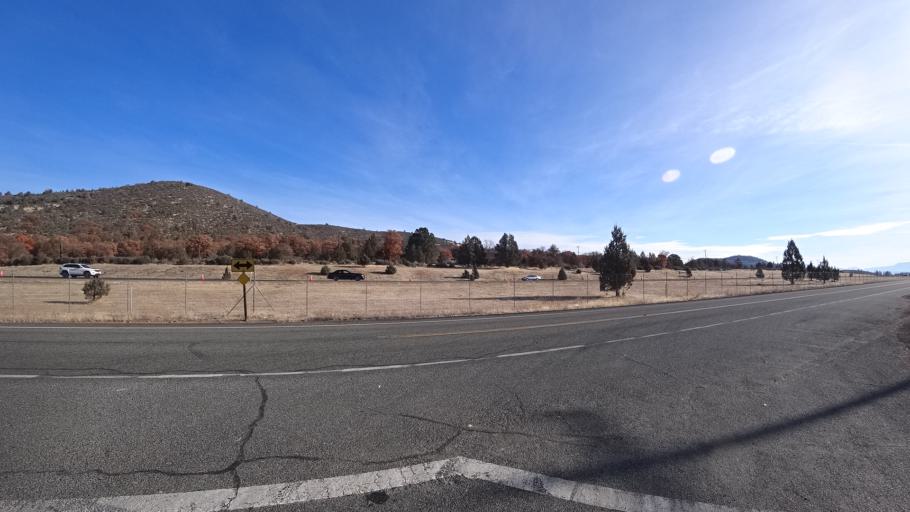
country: US
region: California
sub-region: Siskiyou County
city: Yreka
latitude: 41.6761
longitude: -122.6252
